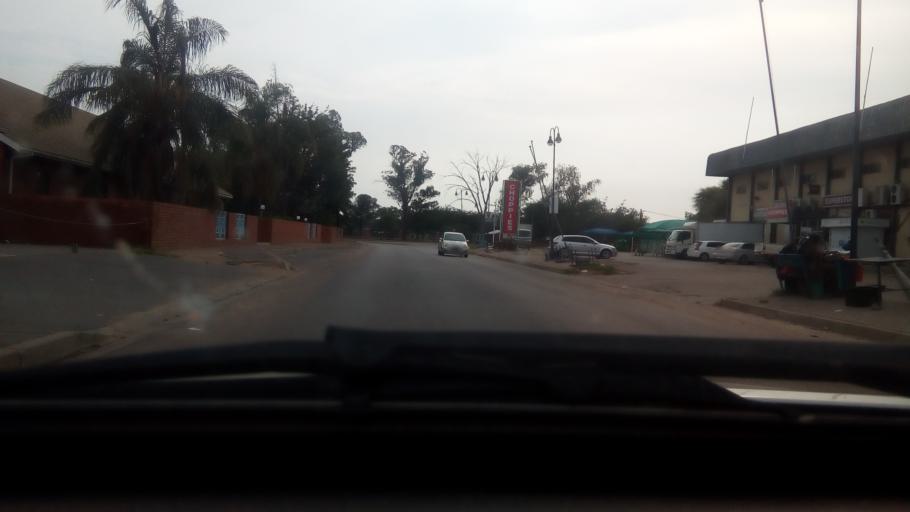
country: BW
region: South East
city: Gaborone
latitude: -24.6672
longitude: 25.9398
